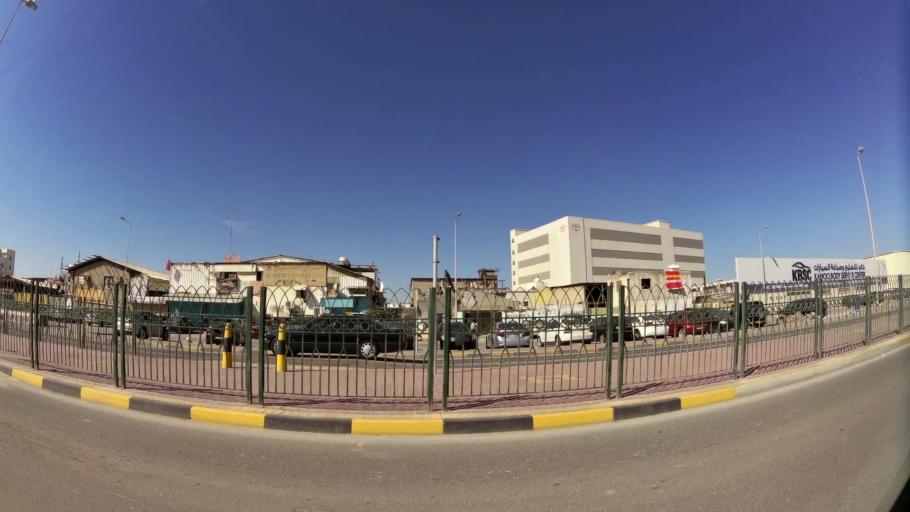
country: BH
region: Muharraq
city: Al Hadd
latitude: 26.2563
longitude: 50.6440
